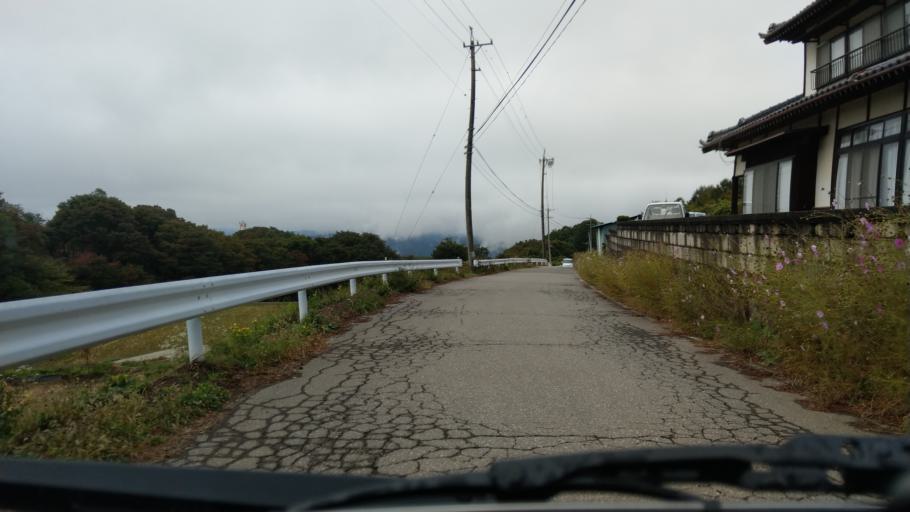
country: JP
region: Nagano
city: Komoro
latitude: 36.3560
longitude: 138.4403
